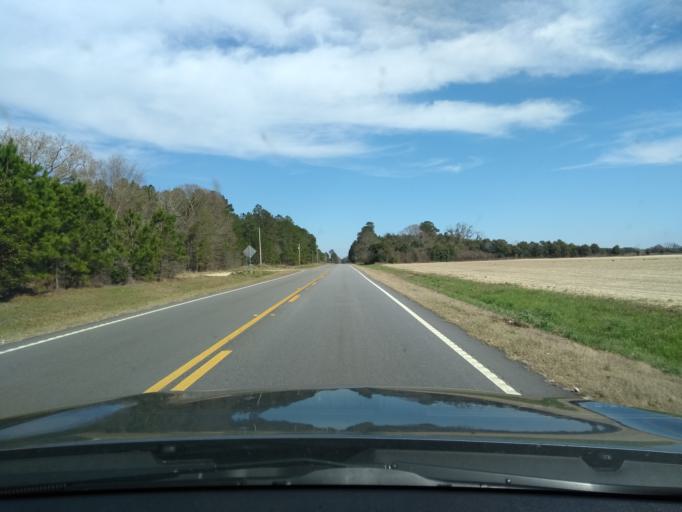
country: US
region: Georgia
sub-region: Bulloch County
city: Brooklet
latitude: 32.4803
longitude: -81.5979
